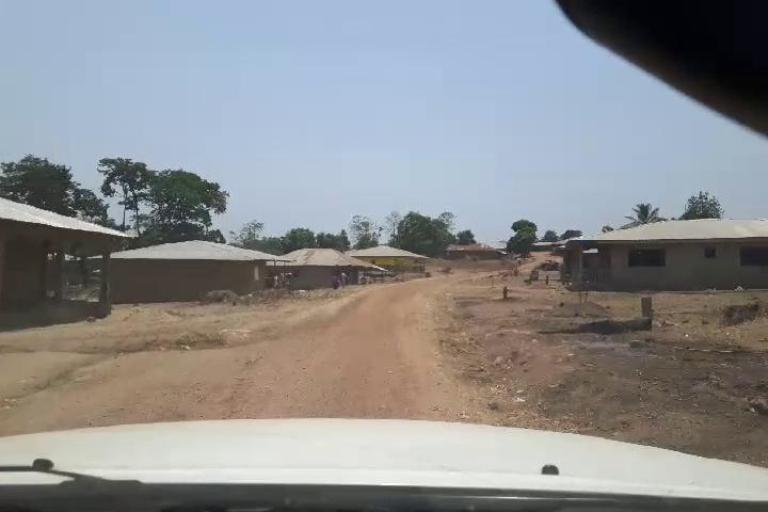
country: SL
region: Northern Province
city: Alikalia
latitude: 9.0629
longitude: -11.4870
